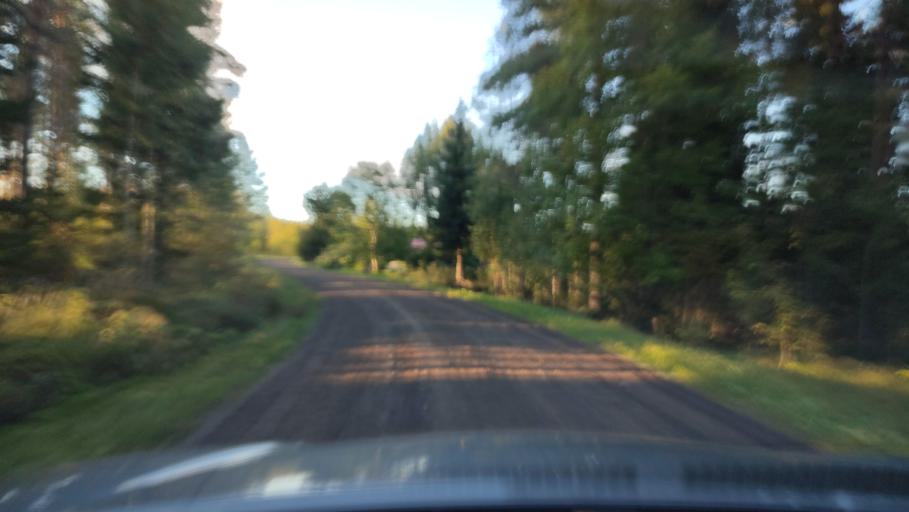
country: FI
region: Southern Ostrobothnia
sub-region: Suupohja
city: Karijoki
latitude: 62.2185
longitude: 21.5728
